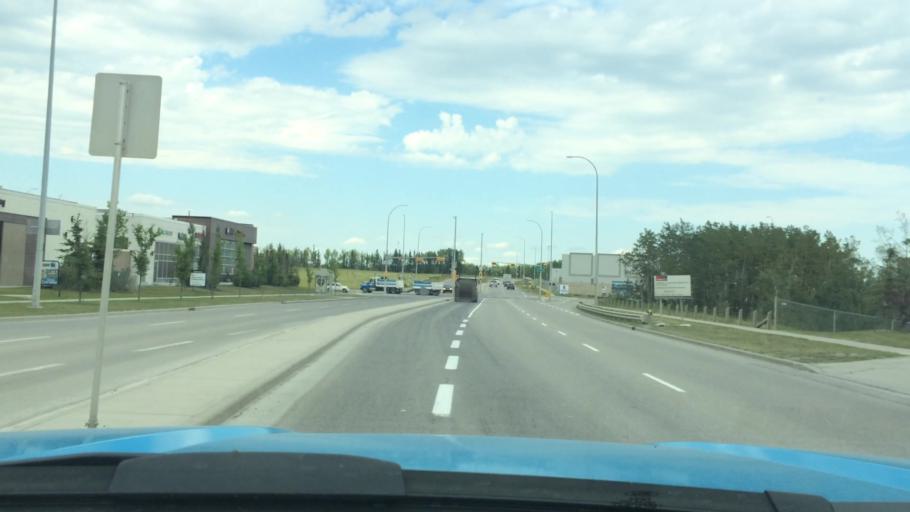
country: CA
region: Alberta
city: Calgary
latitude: 51.1512
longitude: -114.2106
